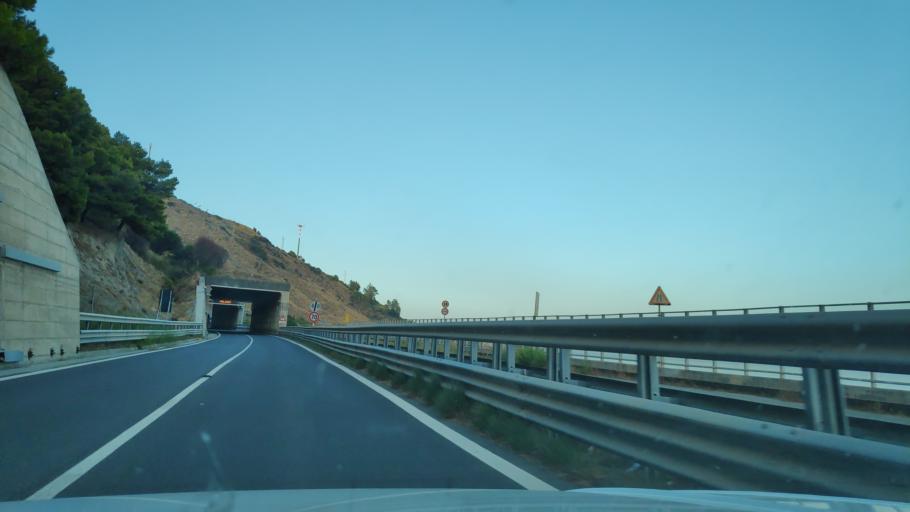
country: IT
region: Calabria
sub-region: Provincia di Reggio Calabria
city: Palizzi Marina
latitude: 37.9202
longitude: 15.9692
